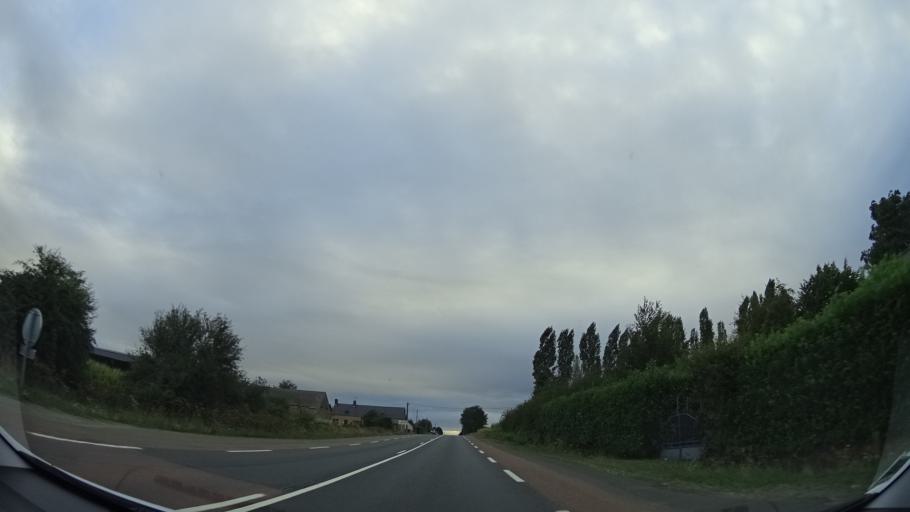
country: FR
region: Pays de la Loire
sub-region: Departement de la Sarthe
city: Trange
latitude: 48.0231
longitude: 0.0933
